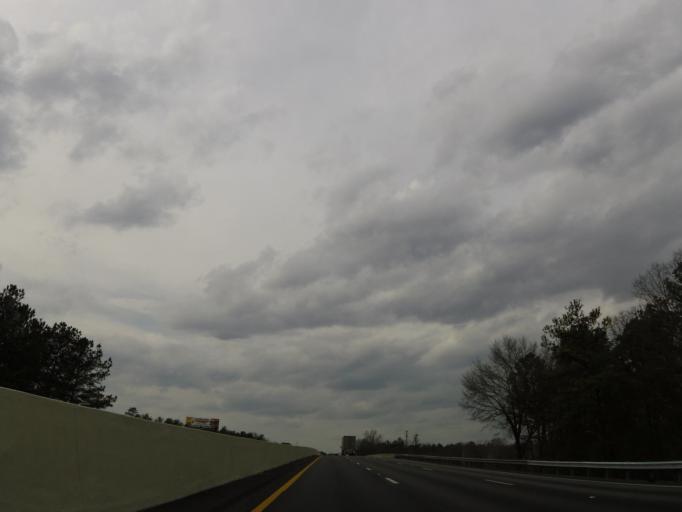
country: US
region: South Carolina
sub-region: Lexington County
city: Pineridge
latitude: 33.9151
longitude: -81.0604
